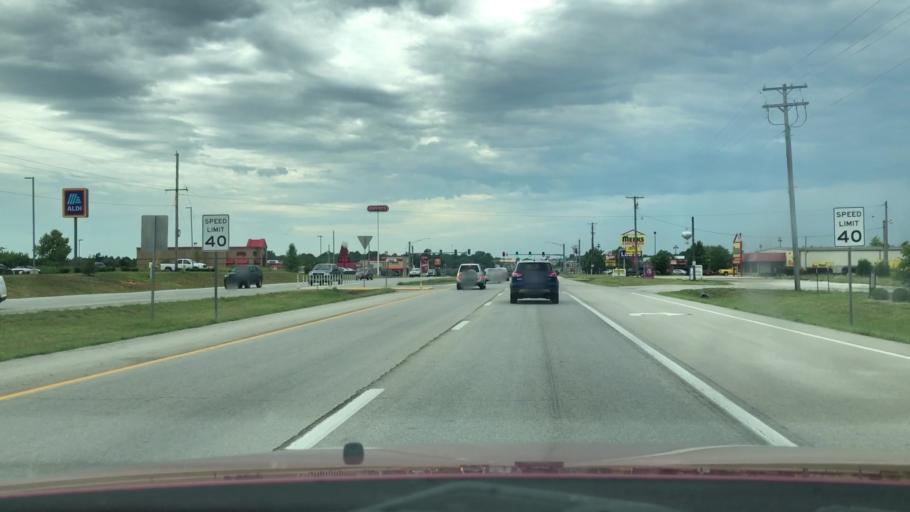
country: US
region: Missouri
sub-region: Greene County
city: Republic
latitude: 37.1330
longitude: -93.4571
